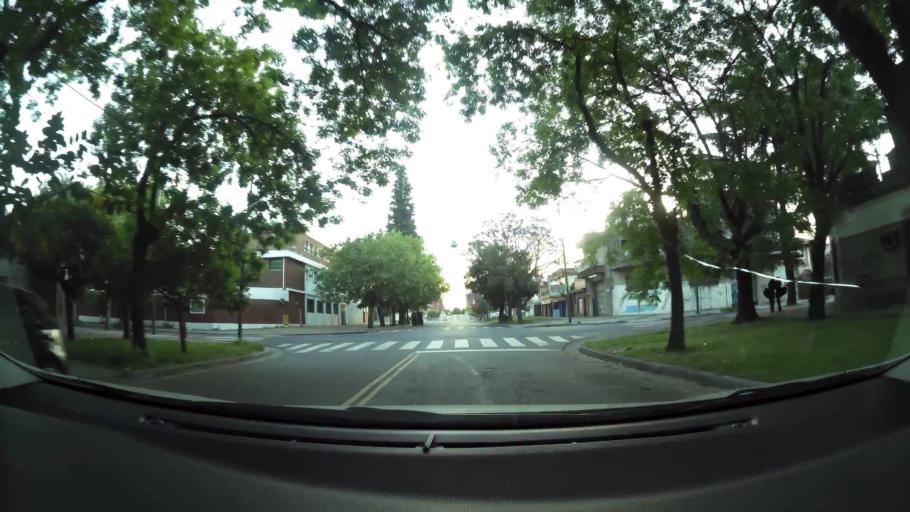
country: AR
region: Buenos Aires F.D.
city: Villa Lugano
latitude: -34.6715
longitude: -58.4692
